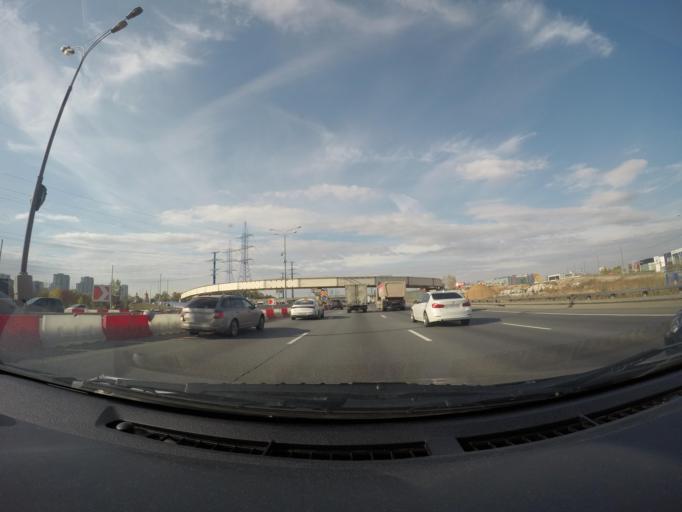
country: RU
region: Moscow
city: Lianozovo
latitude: 55.9089
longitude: 37.5926
